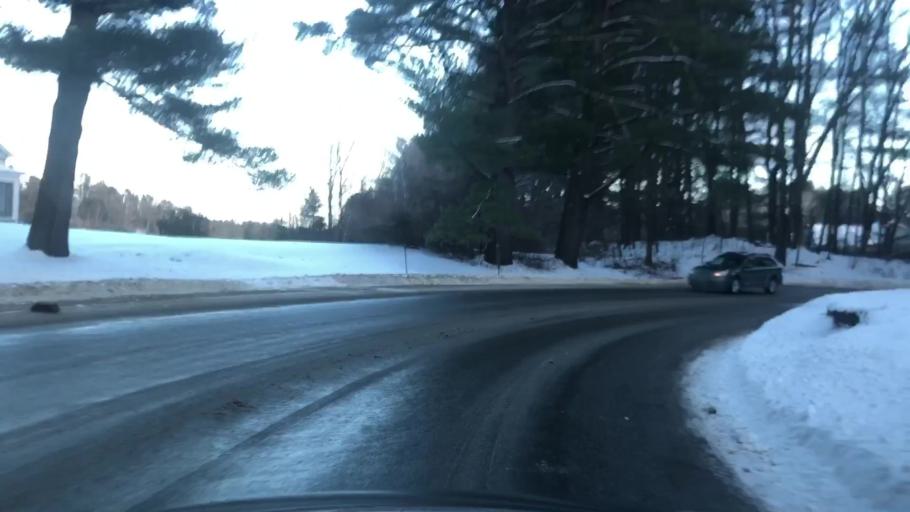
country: US
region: New Hampshire
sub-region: Hillsborough County
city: Milford
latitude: 42.8181
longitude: -71.6596
